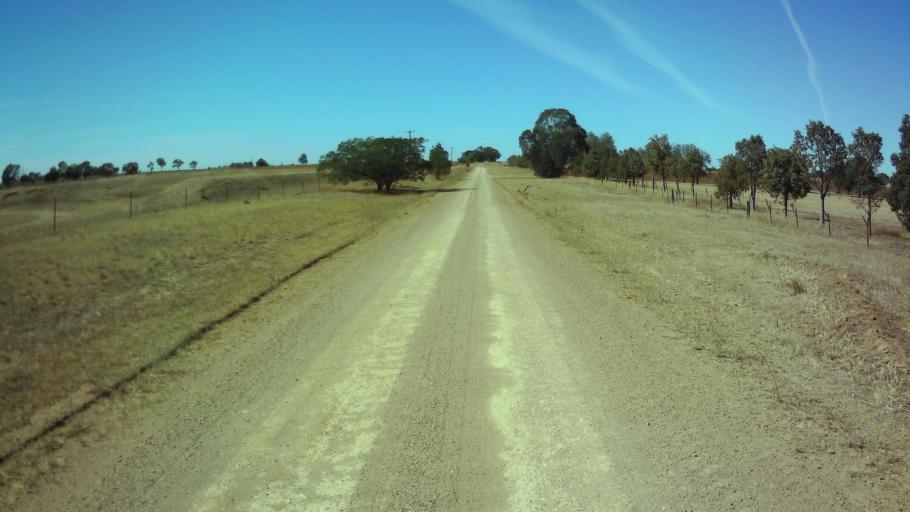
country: AU
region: New South Wales
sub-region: Weddin
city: Grenfell
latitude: -34.0567
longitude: 148.1717
